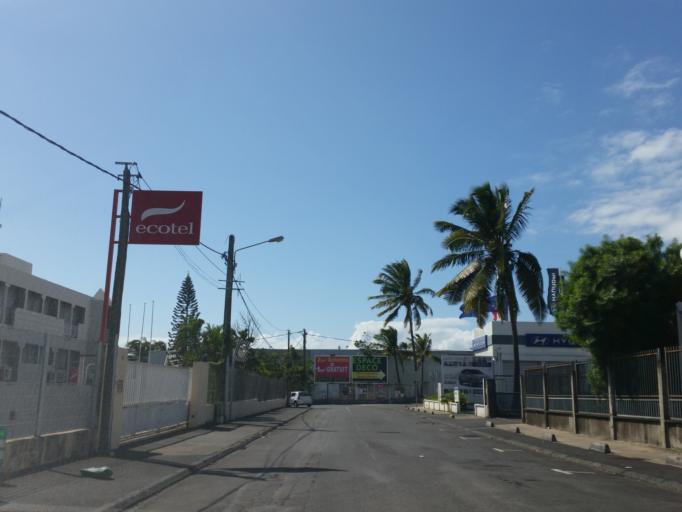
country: RE
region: Reunion
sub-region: Reunion
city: Saint-Denis
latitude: -20.8952
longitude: 55.4968
